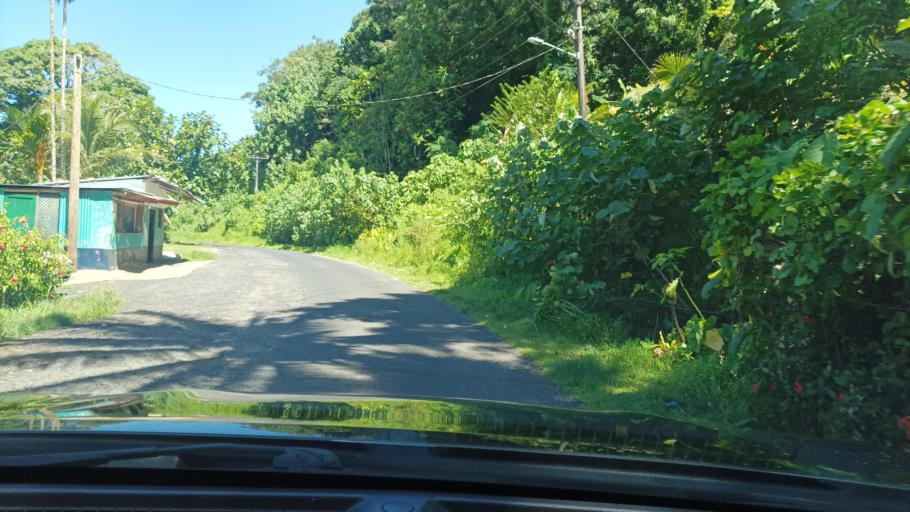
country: FM
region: Pohnpei
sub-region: Madolenihm Municipality
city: Madolenihm Municipality Government
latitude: 6.8559
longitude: 158.2944
